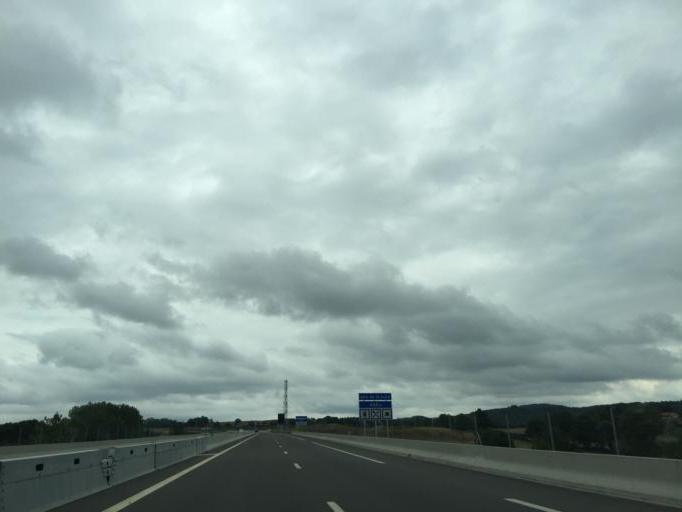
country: FR
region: Rhone-Alpes
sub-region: Departement de la Loire
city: Balbigny
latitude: 45.8469
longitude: 4.2154
